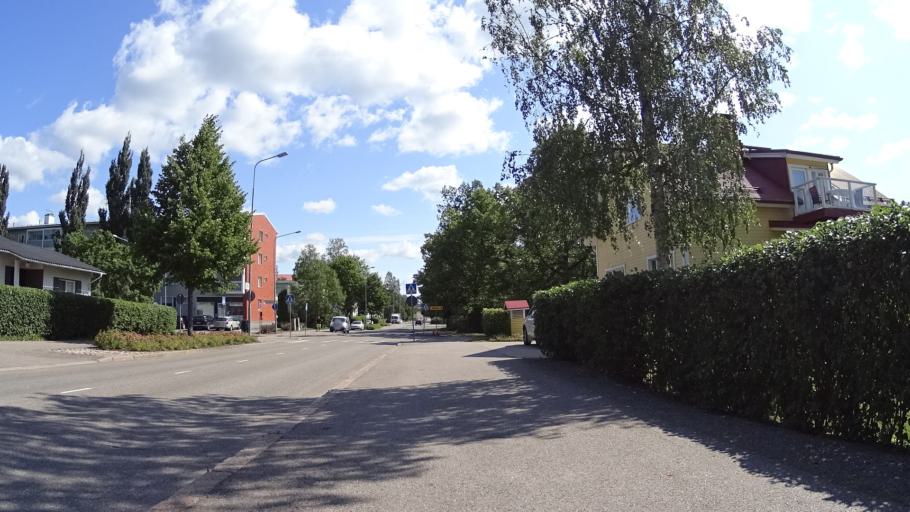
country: FI
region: Uusimaa
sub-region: Helsinki
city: Jaervenpaeae
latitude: 60.4751
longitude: 25.0794
